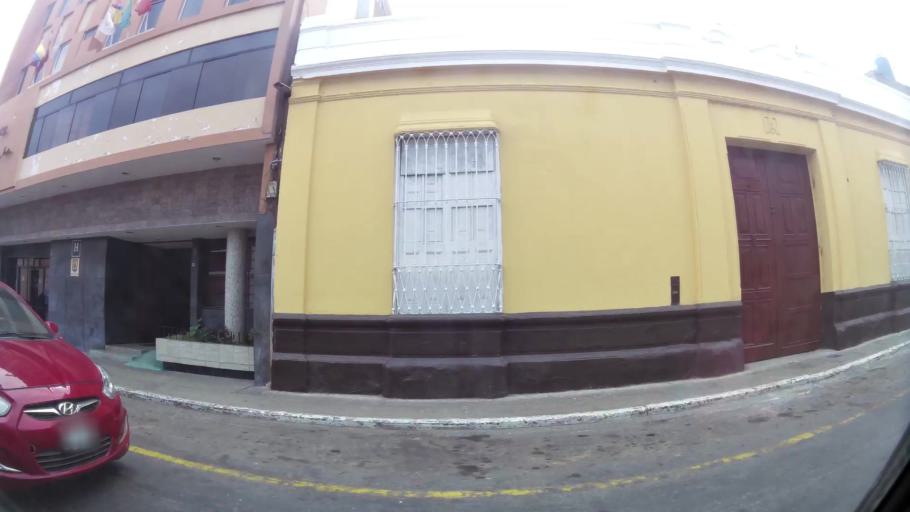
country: PE
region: La Libertad
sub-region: Provincia de Trujillo
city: Trujillo
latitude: -8.1071
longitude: -79.0270
